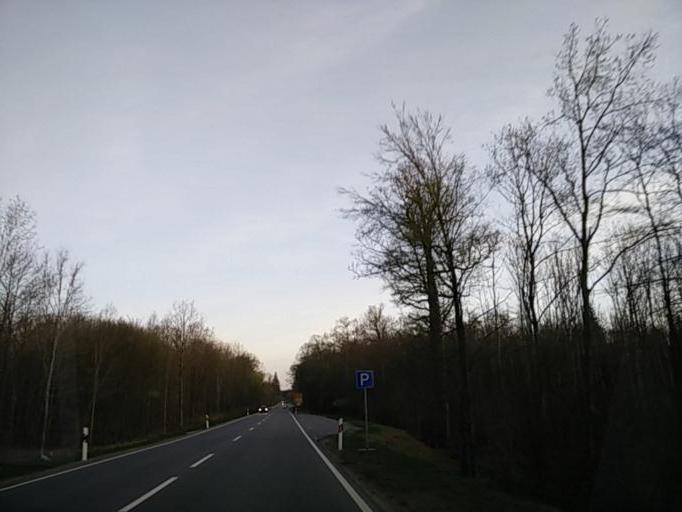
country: DE
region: Baden-Wuerttemberg
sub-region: Regierungsbezirk Stuttgart
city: Weil im Schonbuch
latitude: 48.6009
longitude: 9.0583
